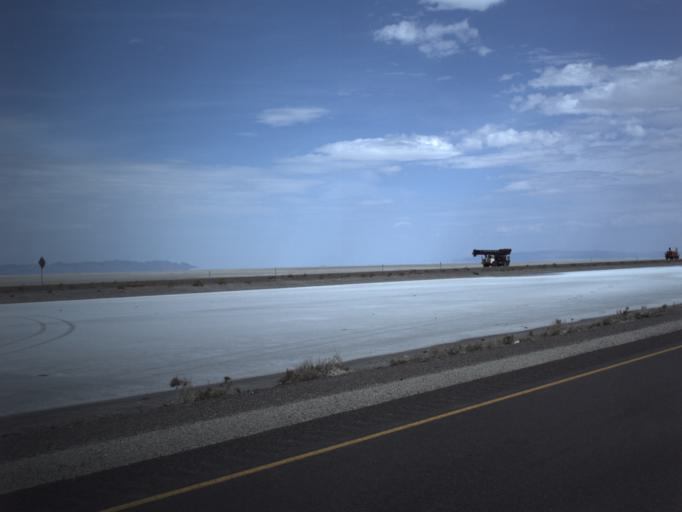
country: US
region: Utah
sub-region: Tooele County
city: Wendover
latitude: 40.7355
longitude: -113.7045
